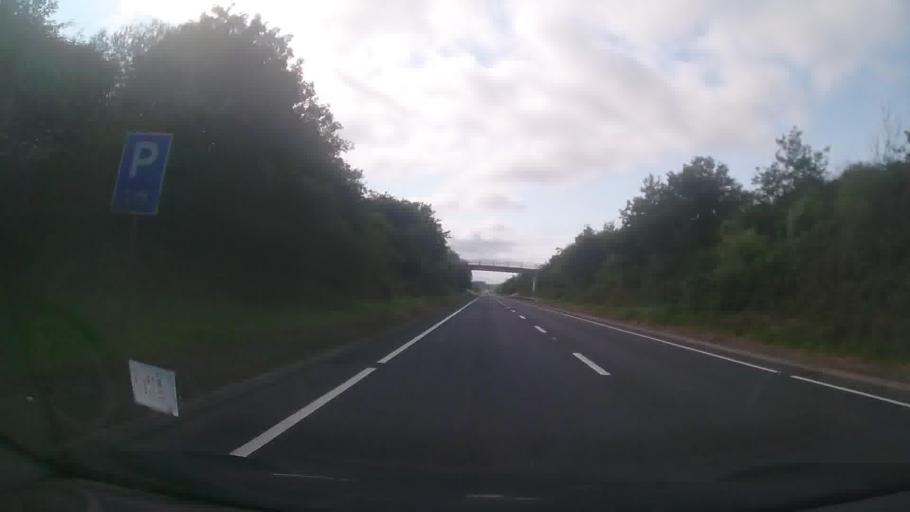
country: GB
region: Wales
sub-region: Pembrokeshire
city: Jeffreyston
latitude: 51.6963
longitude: -4.7926
